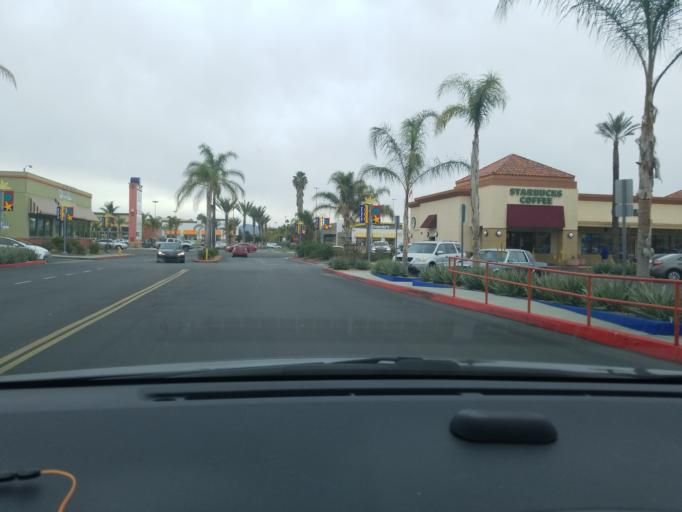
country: US
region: California
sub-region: Riverside County
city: Hemet
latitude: 33.7482
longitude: -116.9959
